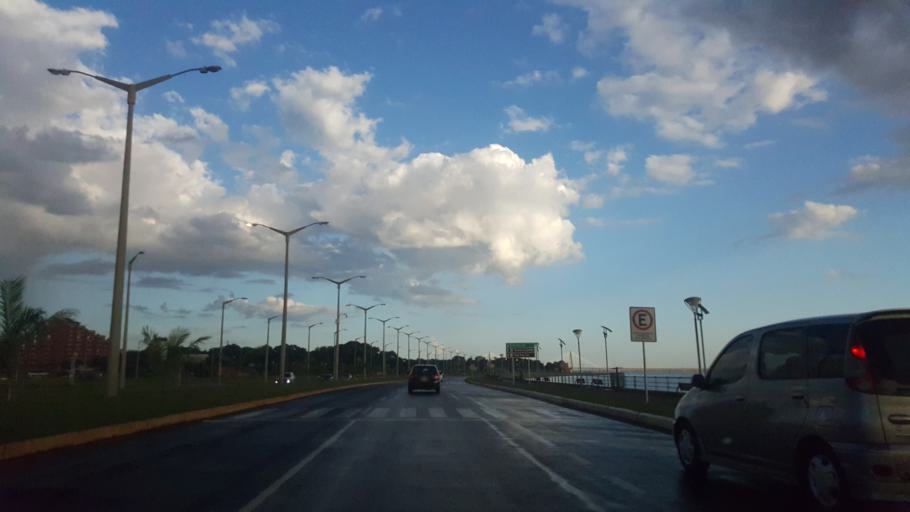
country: PY
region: Itapua
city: Encarnacion
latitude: -27.3454
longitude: -55.8689
